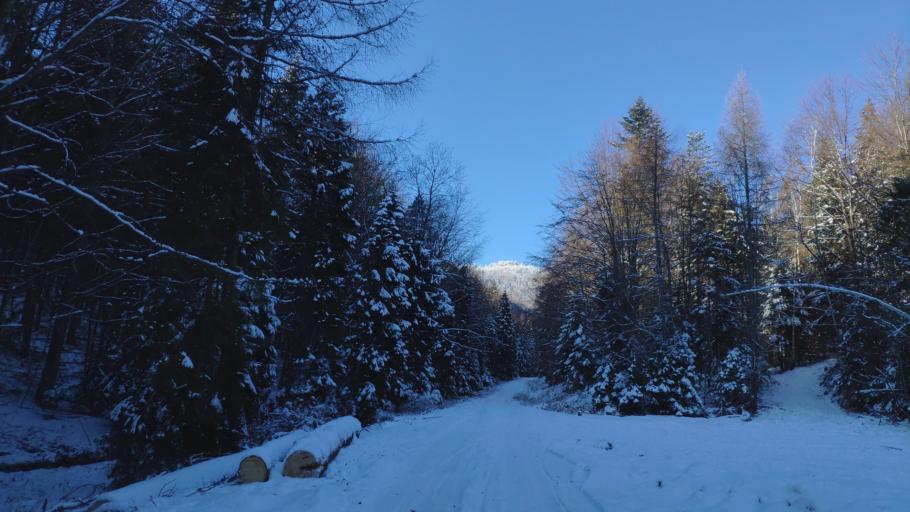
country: SK
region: Kosicky
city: Medzev
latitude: 48.7642
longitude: 20.9652
